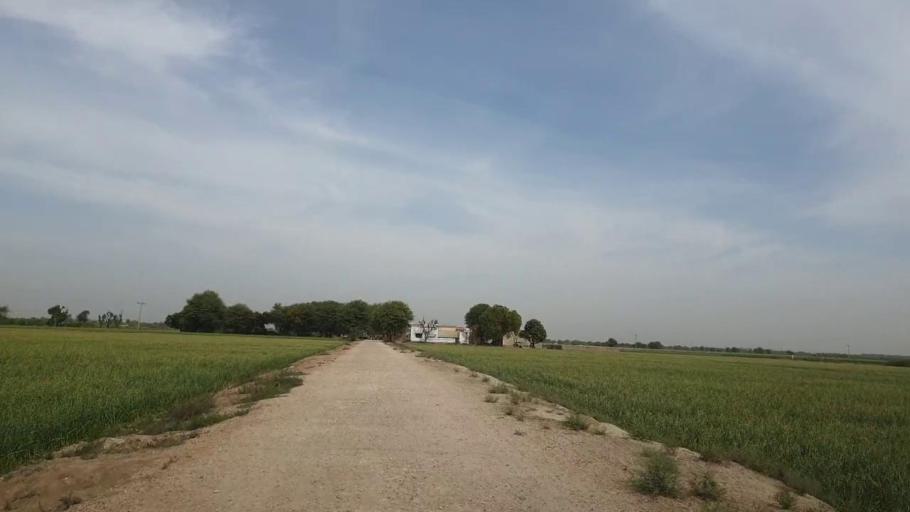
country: PK
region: Sindh
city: Kunri
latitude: 25.1837
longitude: 69.5887
